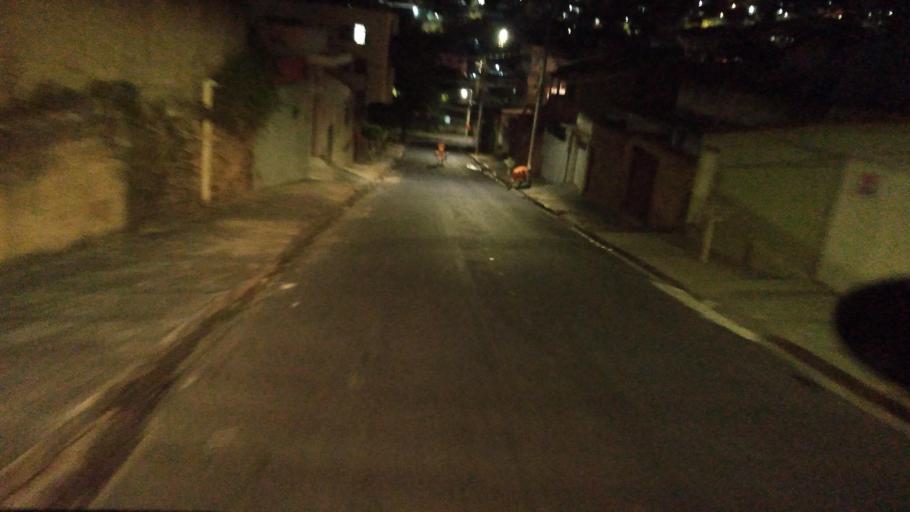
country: BR
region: Minas Gerais
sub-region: Belo Horizonte
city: Belo Horizonte
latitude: -19.8909
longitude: -43.9593
